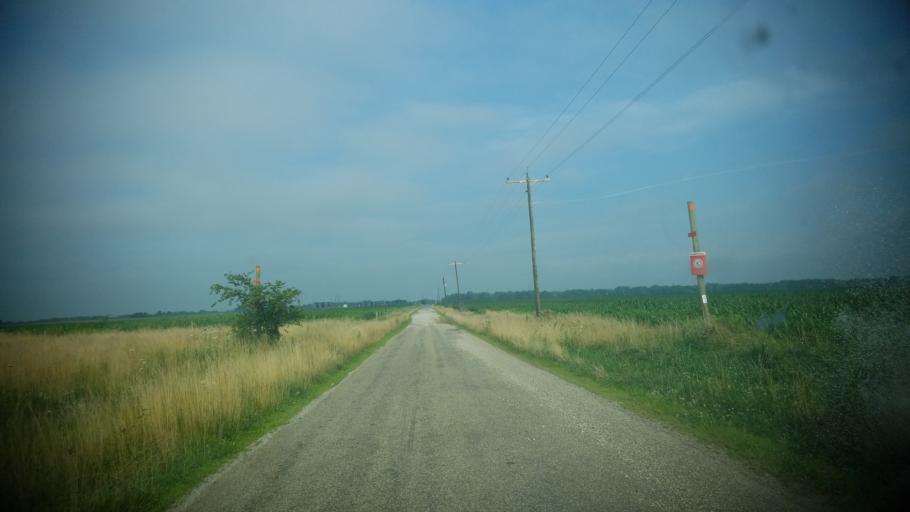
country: US
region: Illinois
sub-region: Clay County
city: Flora
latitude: 38.6015
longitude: -88.3439
